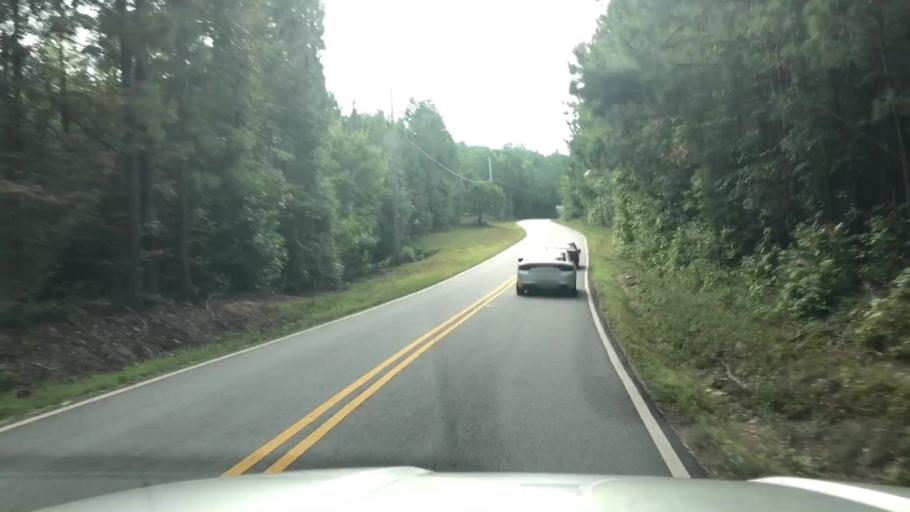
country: US
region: Georgia
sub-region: Bartow County
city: Euharlee
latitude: 34.0465
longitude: -84.8593
